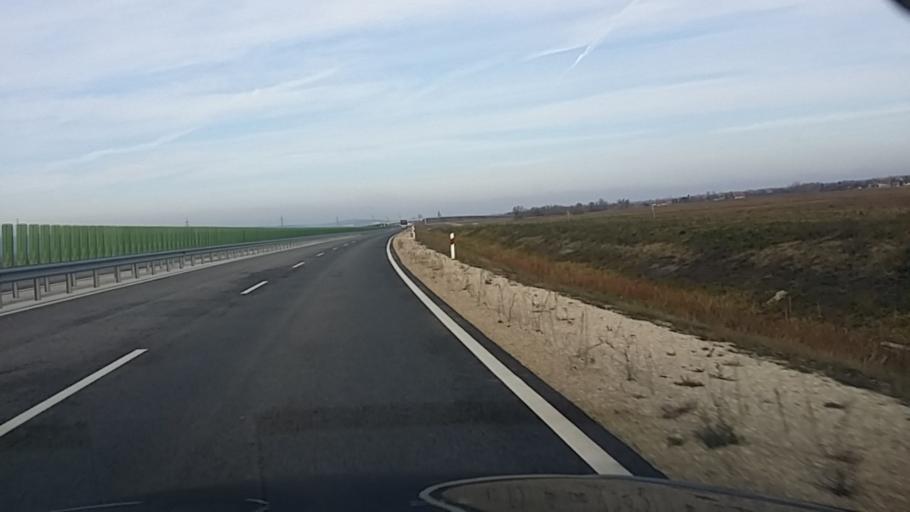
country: HU
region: Fejer
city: Sarszentmihaly
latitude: 47.1928
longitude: 18.3526
